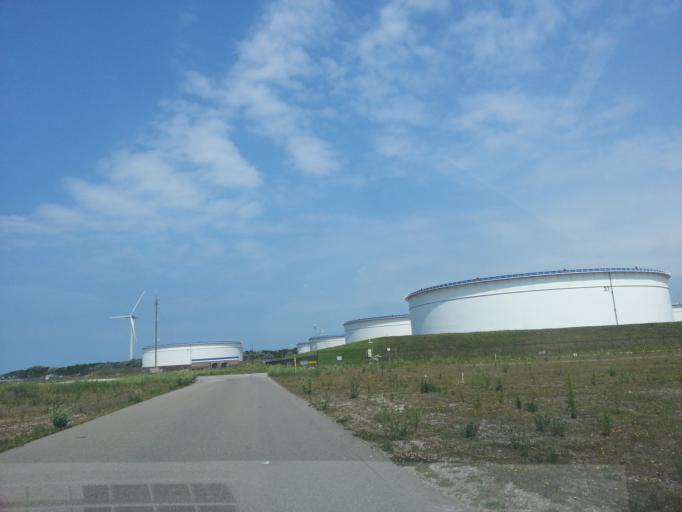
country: NL
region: South Holland
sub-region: Gemeente Rotterdam
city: Hoek van Holland
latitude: 51.9737
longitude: 4.0466
